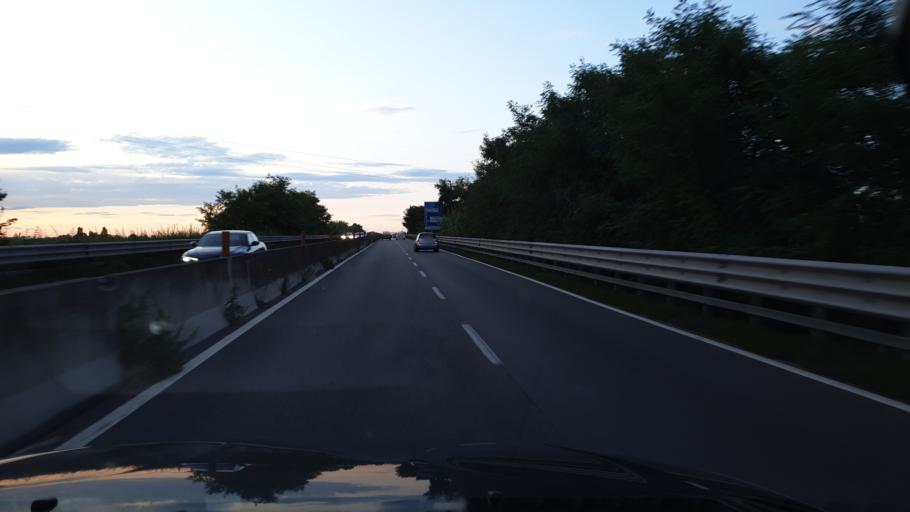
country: IT
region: Emilia-Romagna
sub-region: Provincia di Ravenna
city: Madonna Dell'Albero
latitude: 44.3908
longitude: 12.1868
